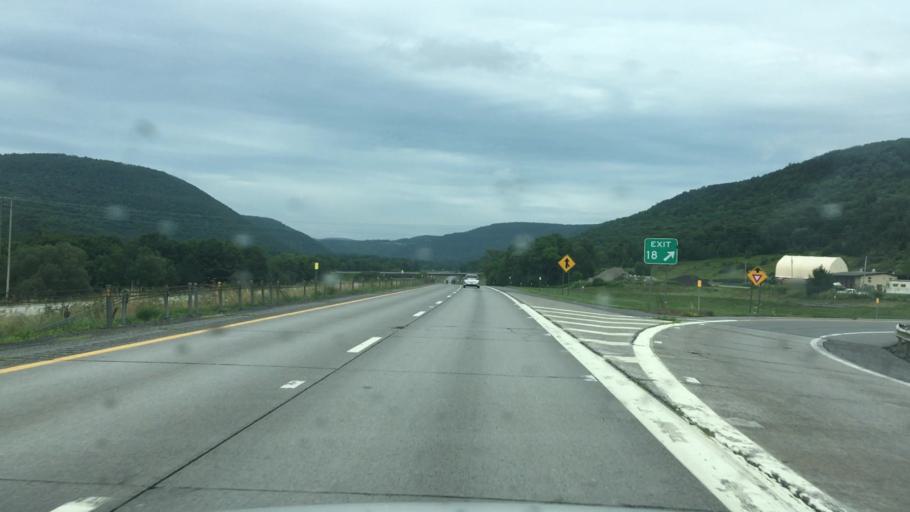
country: US
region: New York
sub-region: Otsego County
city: Worcester
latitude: 42.5423
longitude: -74.8192
